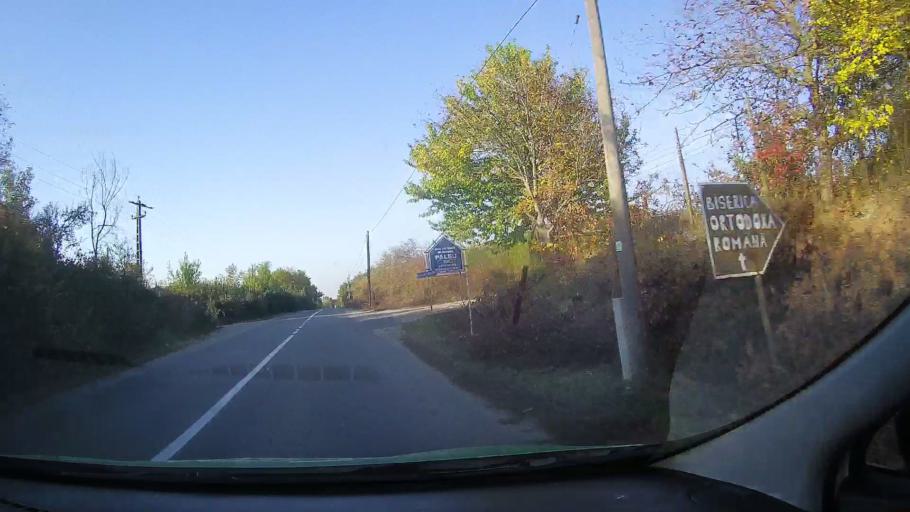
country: RO
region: Bihor
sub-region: Comuna Paleu
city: Paleu
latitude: 47.1046
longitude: 21.9287
